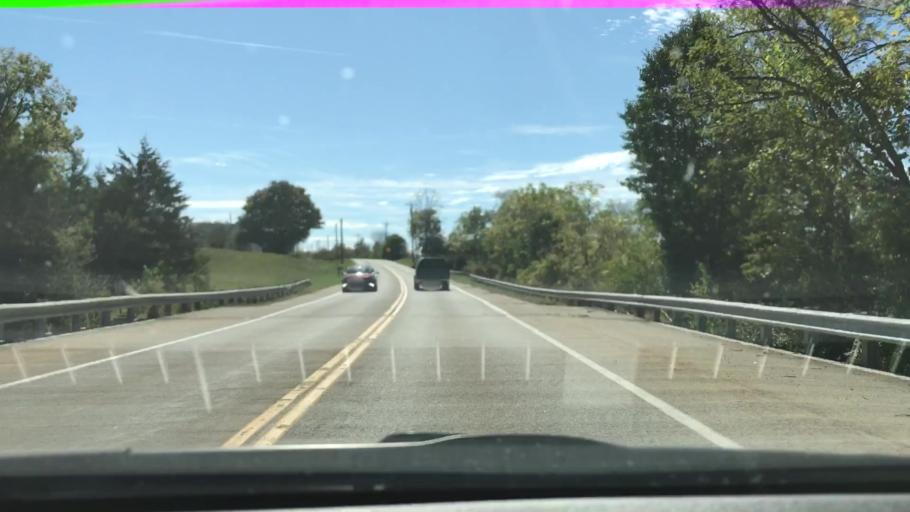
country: US
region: Ohio
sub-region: Butler County
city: Hamilton
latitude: 39.4603
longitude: -84.6276
